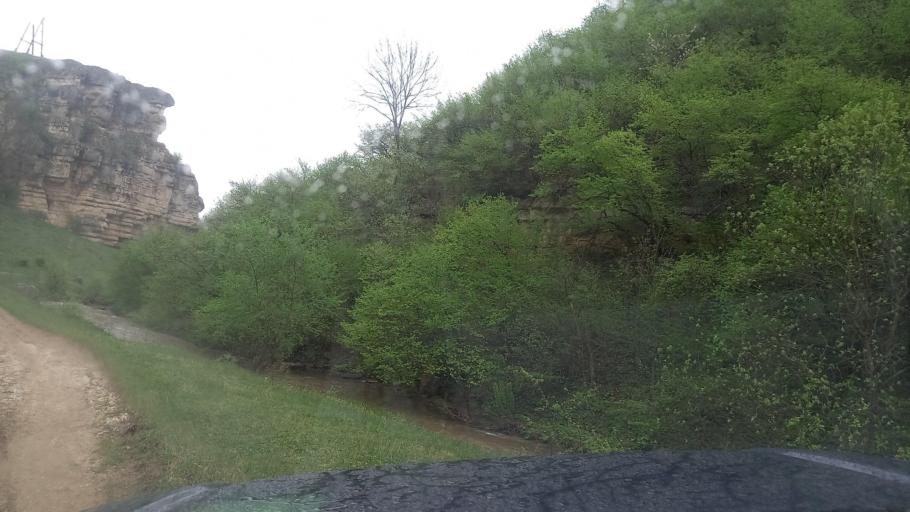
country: RU
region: Stavropol'skiy
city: Kislovodsk
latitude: 43.8853
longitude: 42.6992
